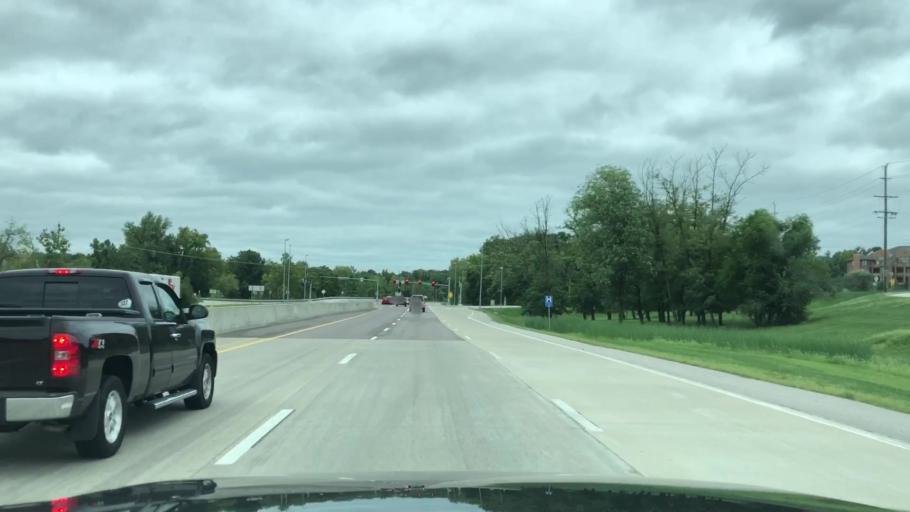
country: US
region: Missouri
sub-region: Saint Louis County
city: Manchester
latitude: 38.6551
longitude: -90.5068
